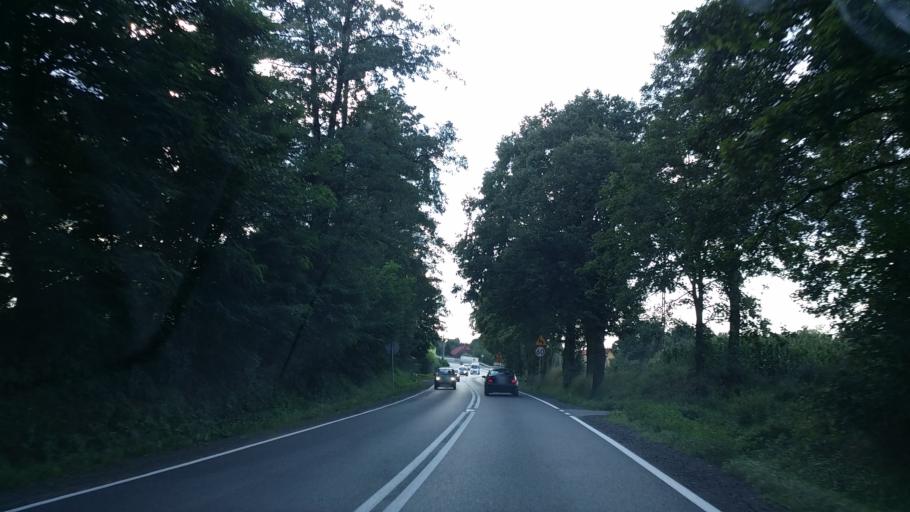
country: PL
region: Lesser Poland Voivodeship
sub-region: Powiat oswiecimski
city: Przeciszow
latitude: 50.0040
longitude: 19.3997
